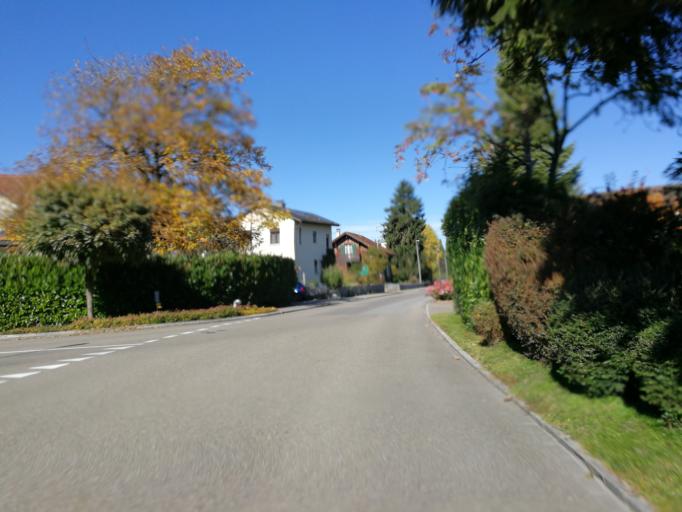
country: CH
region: Saint Gallen
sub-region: Wahlkreis See-Gaster
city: Jona
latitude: 47.2206
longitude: 8.8336
